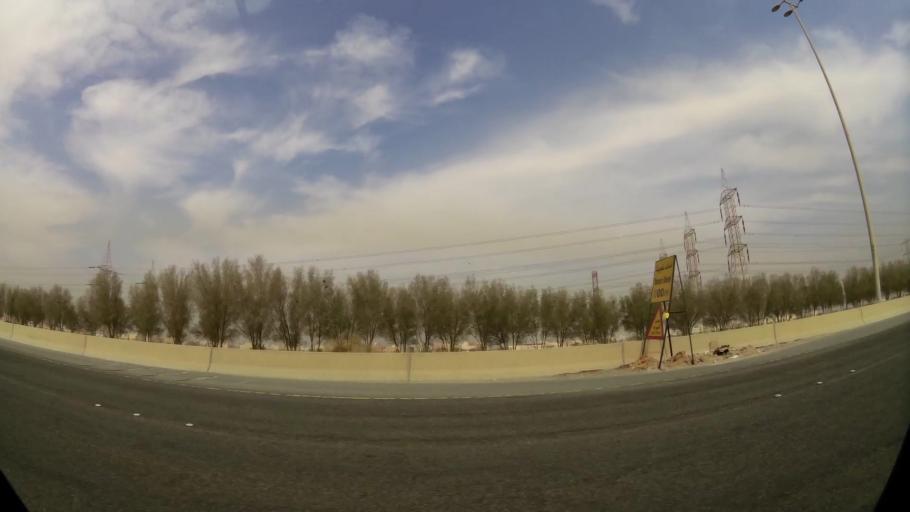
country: KW
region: Muhafazat al Jahra'
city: Al Jahra'
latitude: 29.3295
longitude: 47.7891
